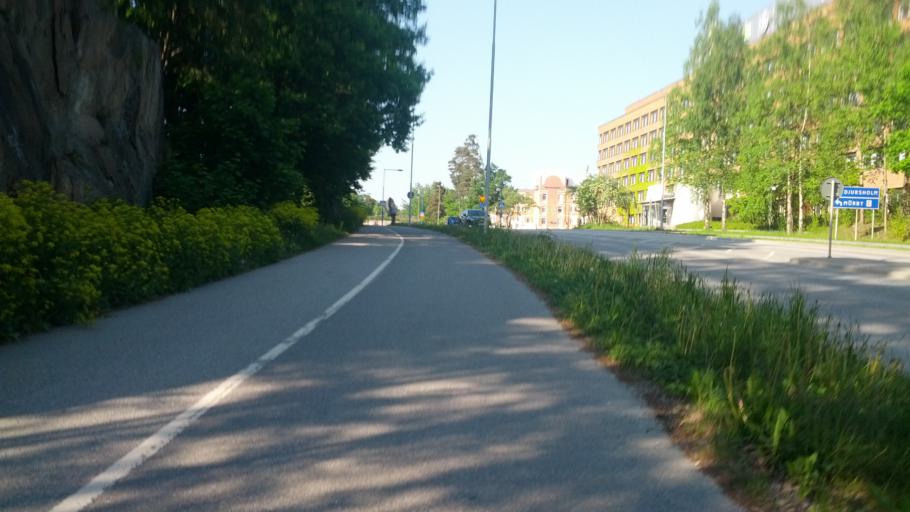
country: SE
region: Stockholm
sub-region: Danderyds Kommun
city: Djursholm
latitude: 59.3944
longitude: 18.0502
